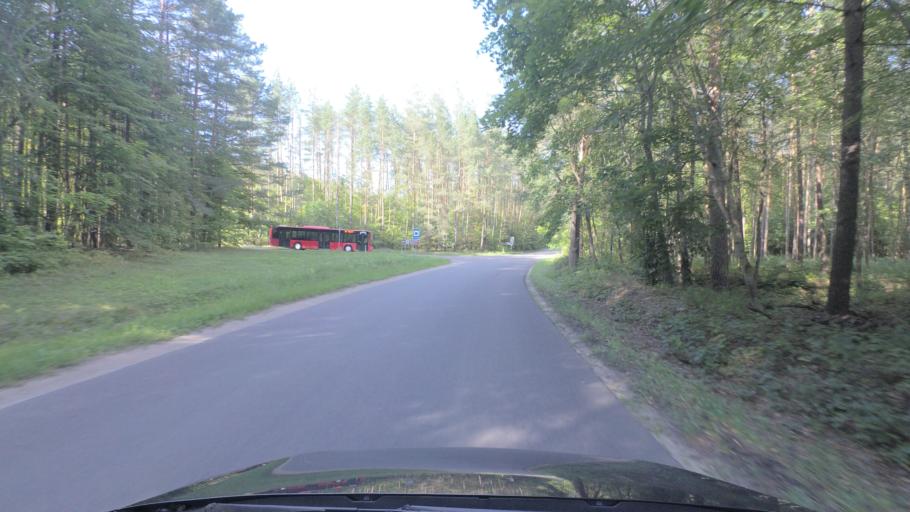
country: LT
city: Nemencine
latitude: 54.8236
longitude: 25.3570
